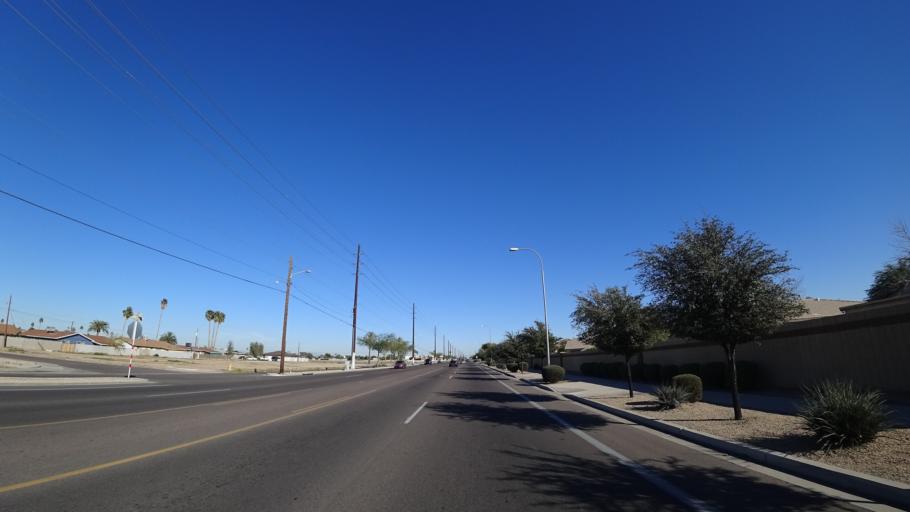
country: US
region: Arizona
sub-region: Maricopa County
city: Phoenix
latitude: 33.3922
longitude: -112.1048
